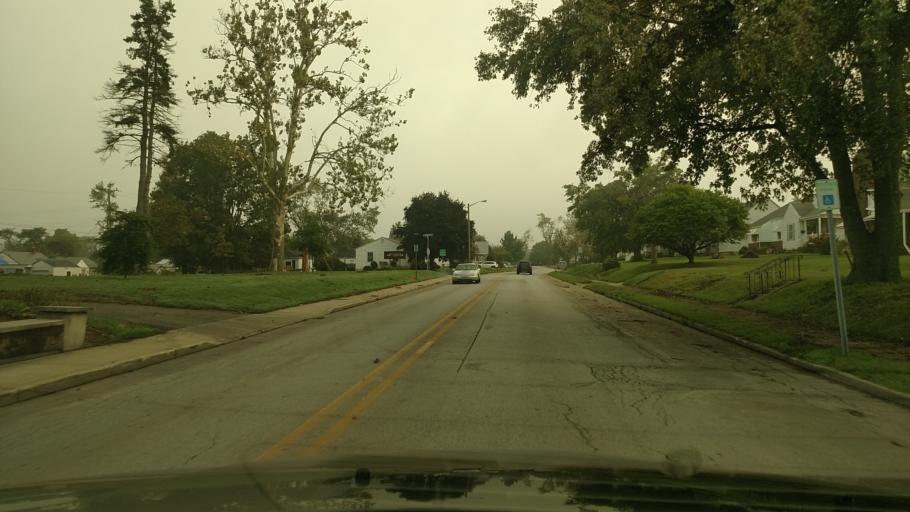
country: US
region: Indiana
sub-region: Howard County
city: Kokomo
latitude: 40.4632
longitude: -86.1365
